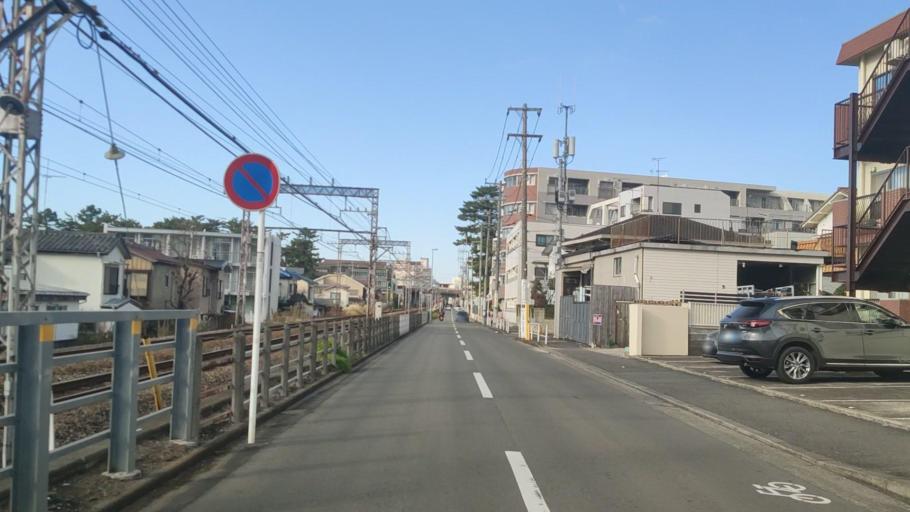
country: JP
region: Kanagawa
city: Minami-rinkan
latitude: 35.4979
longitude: 139.4470
